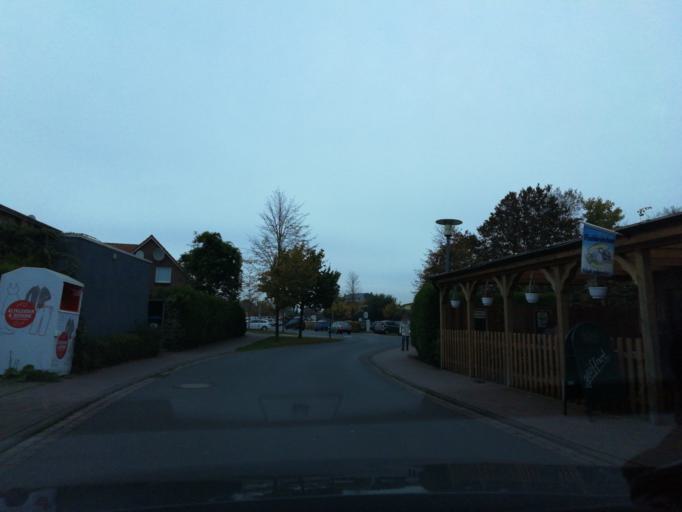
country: DE
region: Lower Saxony
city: Sillenstede
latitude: 53.6292
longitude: 8.0274
